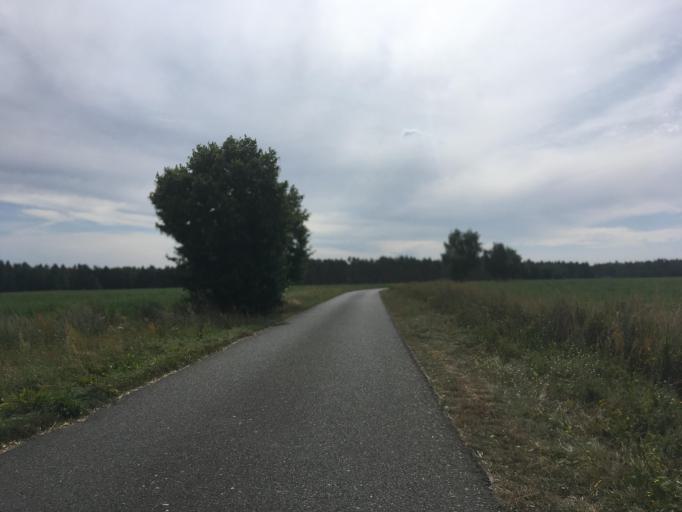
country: DE
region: Saxony-Anhalt
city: Pretzsch
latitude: 51.6904
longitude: 12.8144
